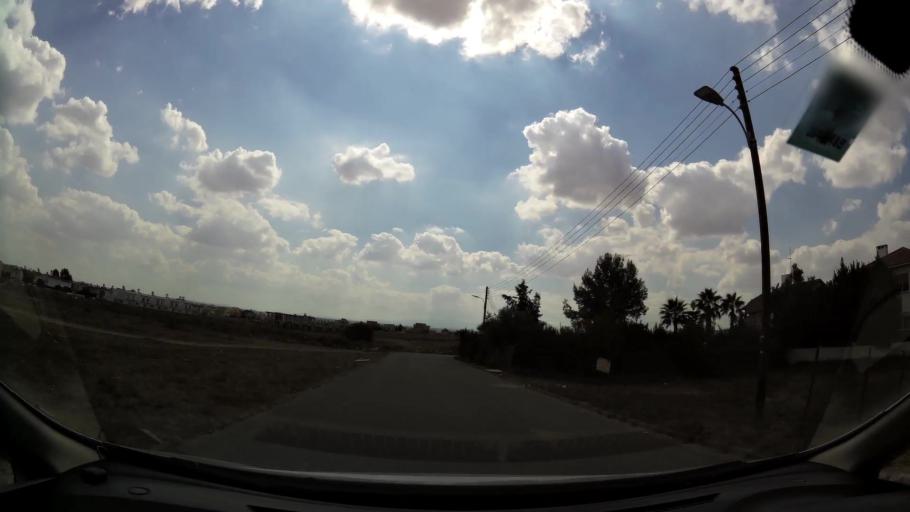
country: CY
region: Lefkosia
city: Nicosia
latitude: 35.2253
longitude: 33.2923
